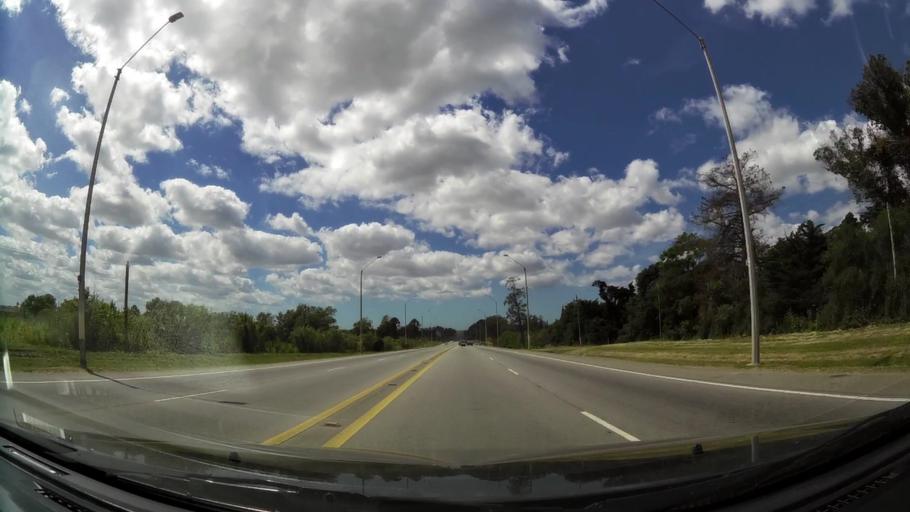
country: UY
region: Canelones
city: Colonia Nicolich
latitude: -34.8014
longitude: -56.0565
